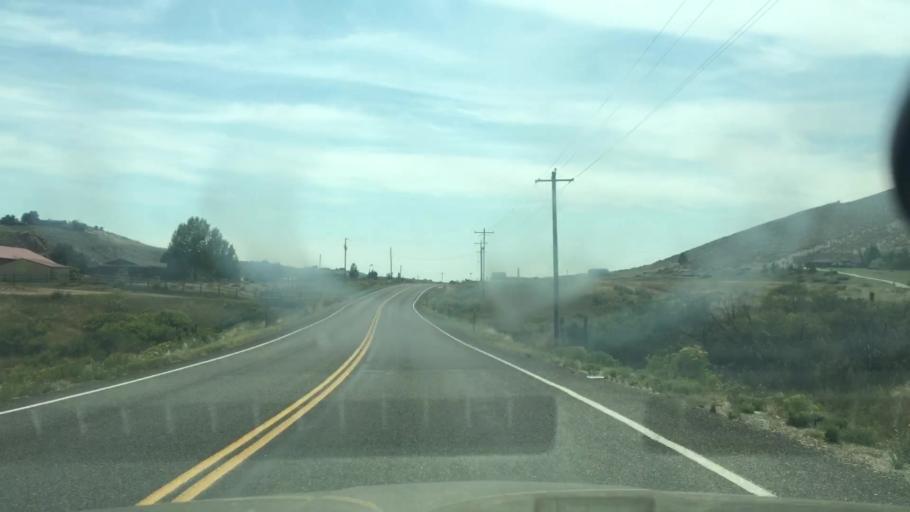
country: US
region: Colorado
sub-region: Larimer County
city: Campion
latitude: 40.3658
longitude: -105.1887
